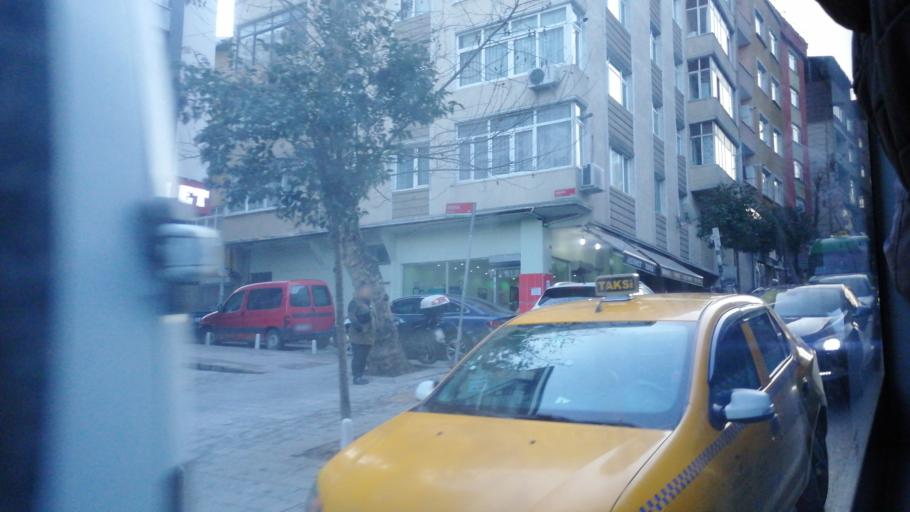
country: TR
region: Istanbul
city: Sisli
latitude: 41.0829
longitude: 28.9894
